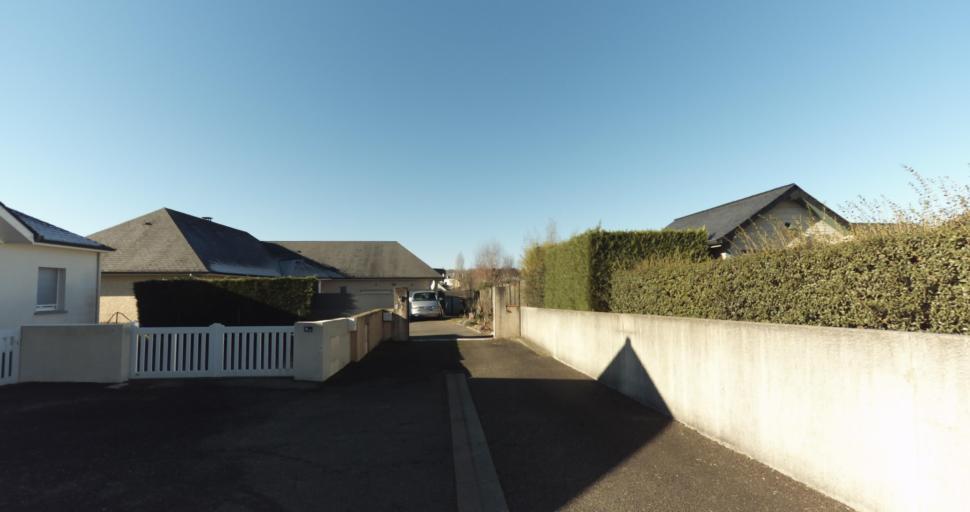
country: FR
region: Aquitaine
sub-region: Departement des Pyrenees-Atlantiques
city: Morlaas
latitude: 43.3452
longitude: -0.2576
